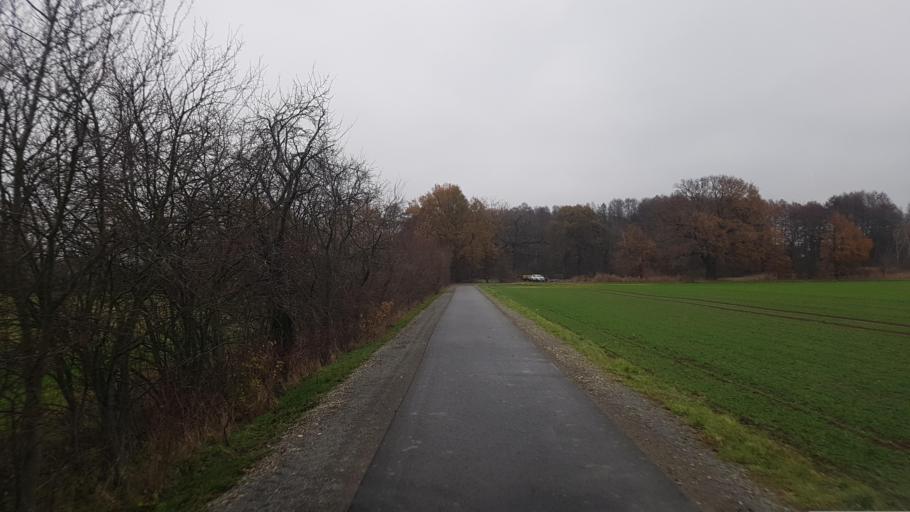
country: DE
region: Brandenburg
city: Crinitz
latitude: 51.7578
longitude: 13.7989
